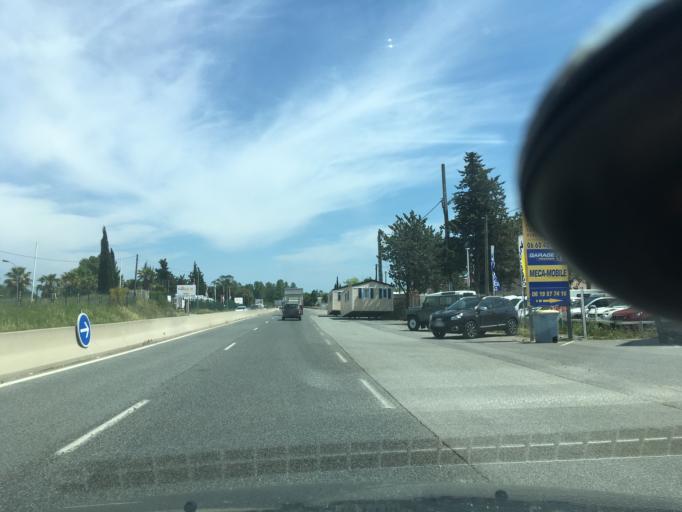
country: FR
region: Provence-Alpes-Cote d'Azur
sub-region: Departement du Var
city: Roquebrune-sur-Argens
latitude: 43.4633
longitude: 6.6423
